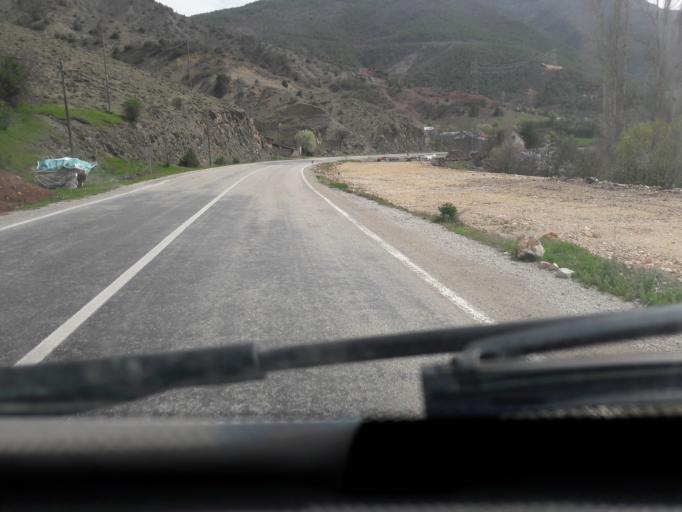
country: TR
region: Gumushane
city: Kale
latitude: 40.4003
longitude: 39.6063
